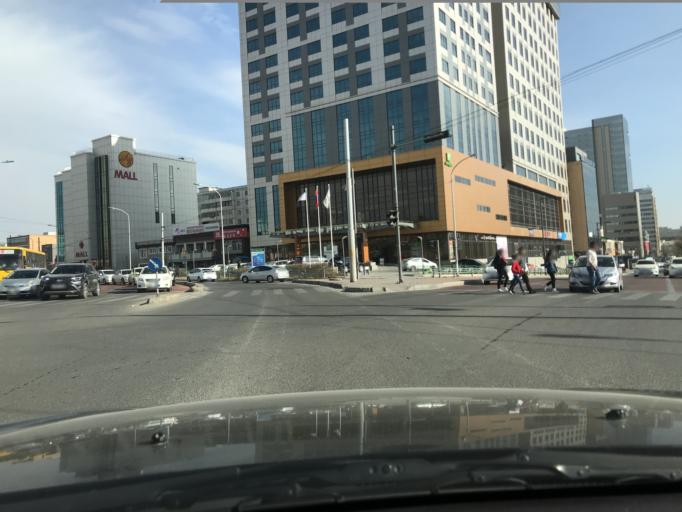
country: MN
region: Ulaanbaatar
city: Ulaanbaatar
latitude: 47.9215
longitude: 106.9005
